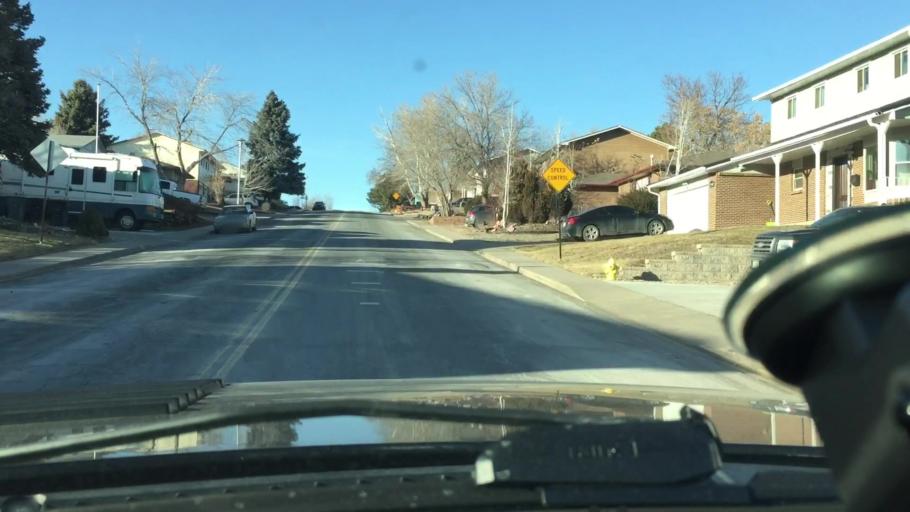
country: US
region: Colorado
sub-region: Adams County
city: Northglenn
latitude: 39.8762
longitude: -105.0056
